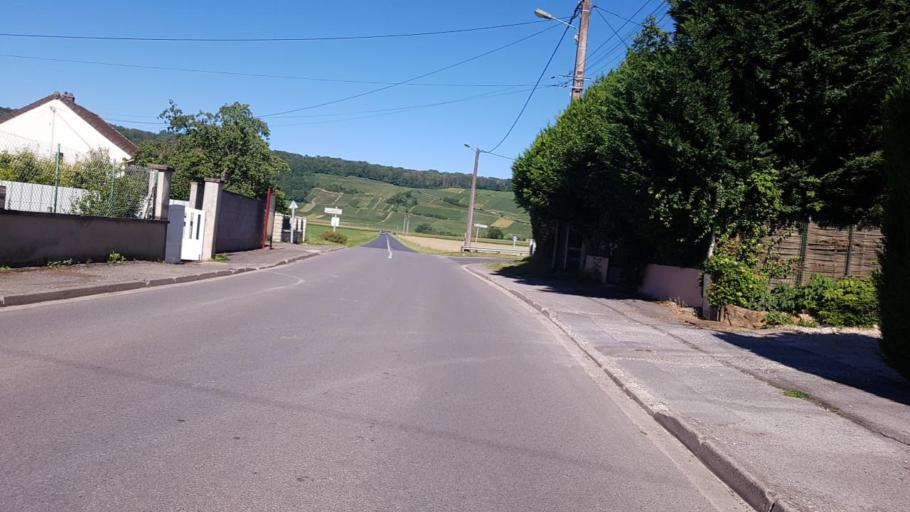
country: FR
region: Picardie
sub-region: Departement de l'Aisne
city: Chezy-sur-Marne
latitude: 49.0023
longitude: 3.3588
